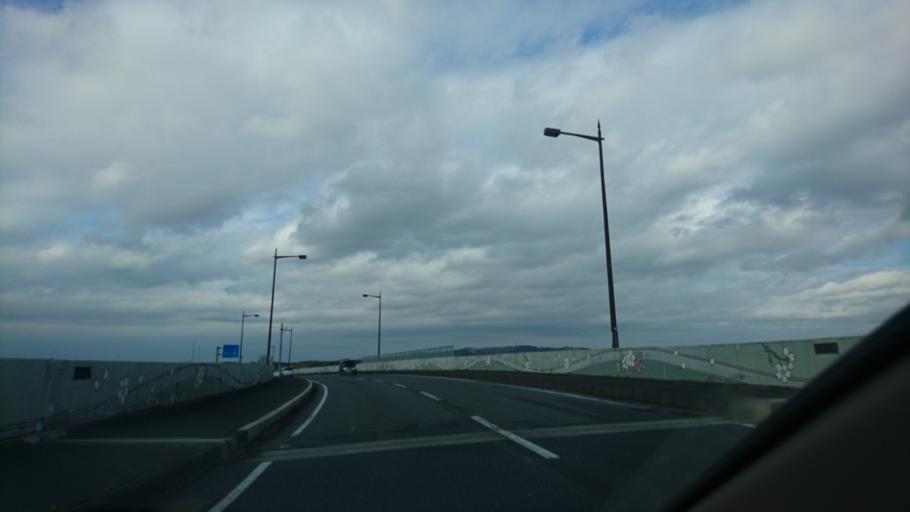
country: JP
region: Miyagi
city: Wakuya
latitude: 38.5460
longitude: 141.1080
